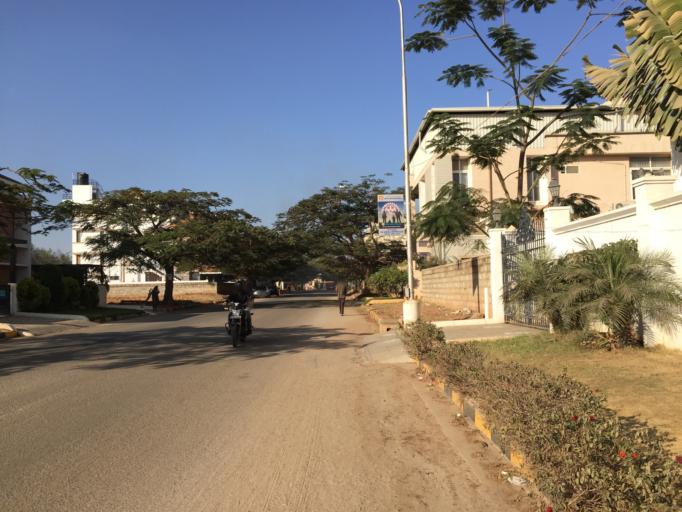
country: IN
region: Karnataka
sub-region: Bangalore Urban
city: Yelahanka
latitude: 13.0556
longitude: 77.6256
